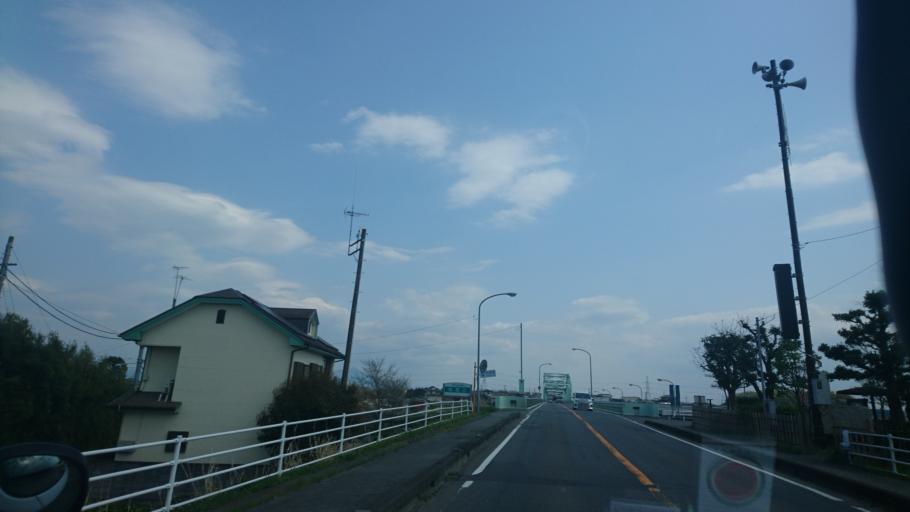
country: JP
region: Ibaraki
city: Yuki
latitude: 36.2785
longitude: 139.9047
